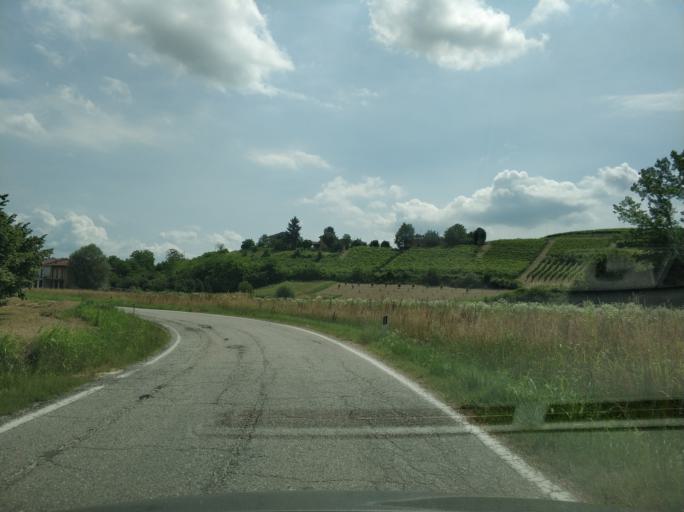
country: IT
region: Piedmont
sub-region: Provincia di Cuneo
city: Santo Stefano Roero
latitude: 44.7841
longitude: 7.9638
